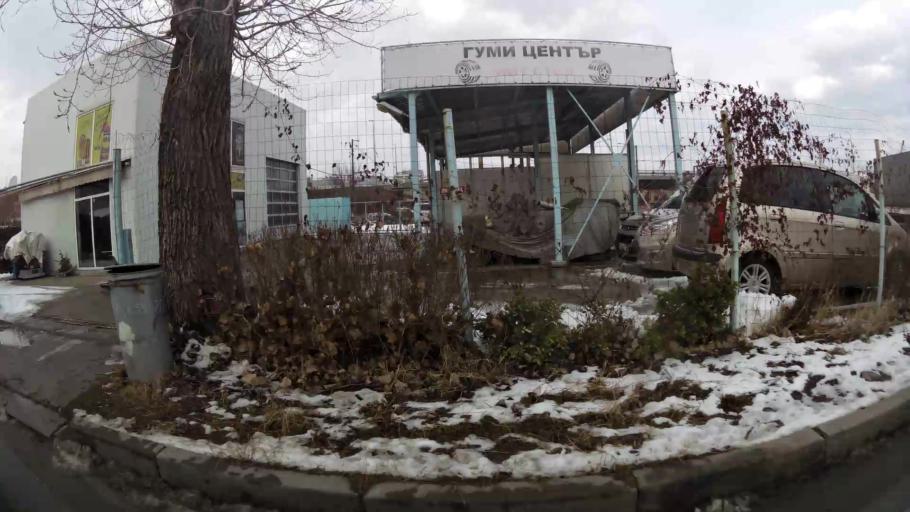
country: BG
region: Sofia-Capital
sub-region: Stolichna Obshtina
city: Sofia
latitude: 42.7082
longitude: 23.3729
